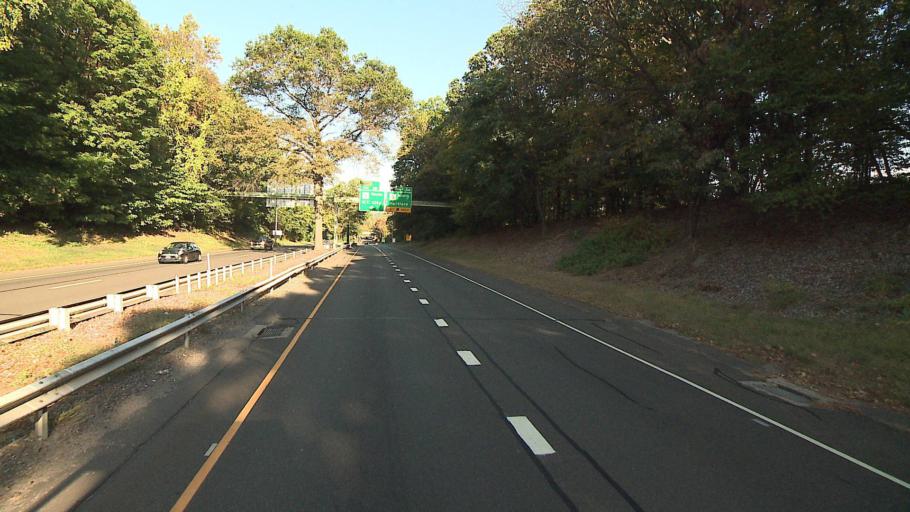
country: US
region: Connecticut
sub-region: New Haven County
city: City of Milford (balance)
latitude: 41.2437
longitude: -73.0818
